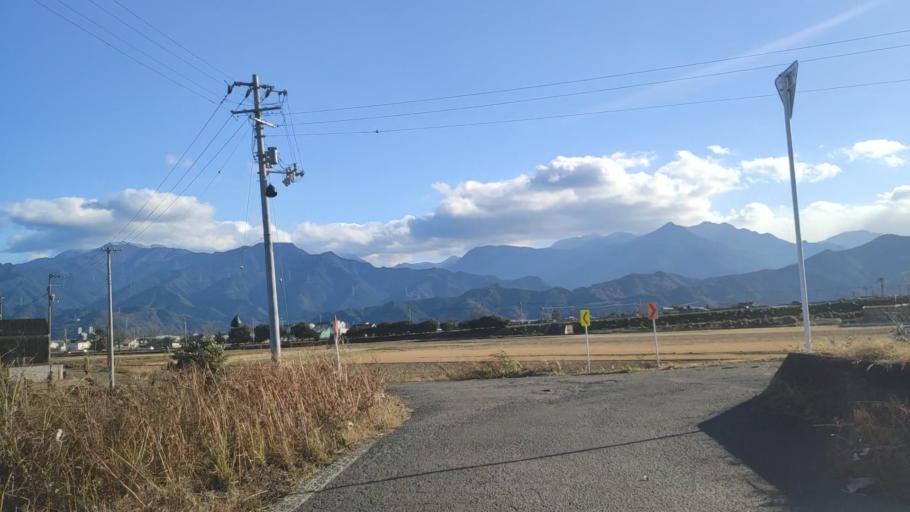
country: JP
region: Ehime
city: Saijo
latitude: 33.9208
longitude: 133.1565
